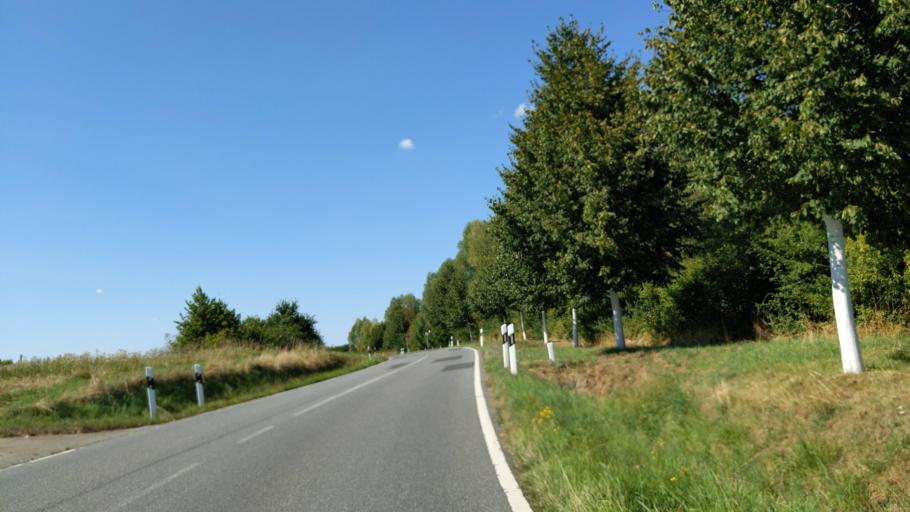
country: DE
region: Mecklenburg-Vorpommern
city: Selmsdorf
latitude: 53.8381
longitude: 10.9169
